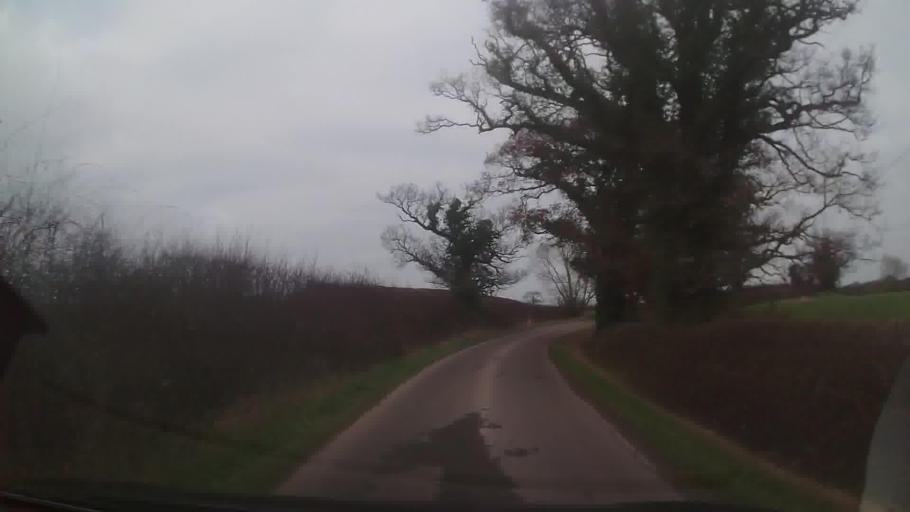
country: GB
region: England
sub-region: Shropshire
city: Petton
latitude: 52.8221
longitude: -2.7948
